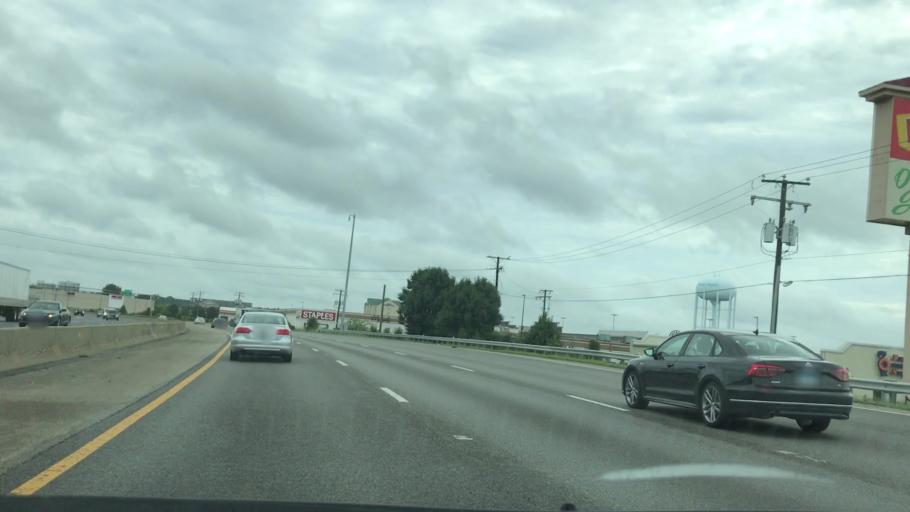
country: US
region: Virginia
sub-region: City of Petersburg
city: Petersburg
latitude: 37.2446
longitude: -77.3934
